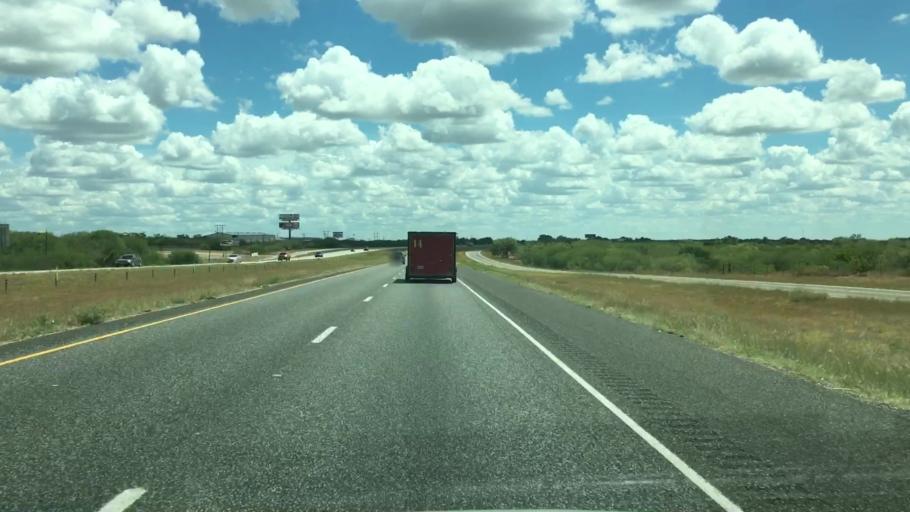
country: US
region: Texas
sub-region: Atascosa County
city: Pleasanton
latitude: 28.8899
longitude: -98.4089
